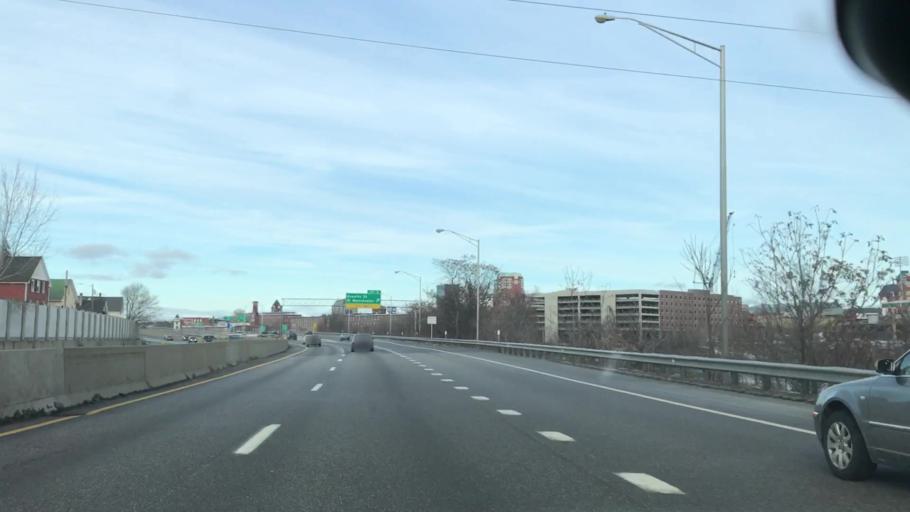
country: US
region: New Hampshire
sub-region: Hillsborough County
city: Manchester
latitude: 42.9793
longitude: -71.4721
